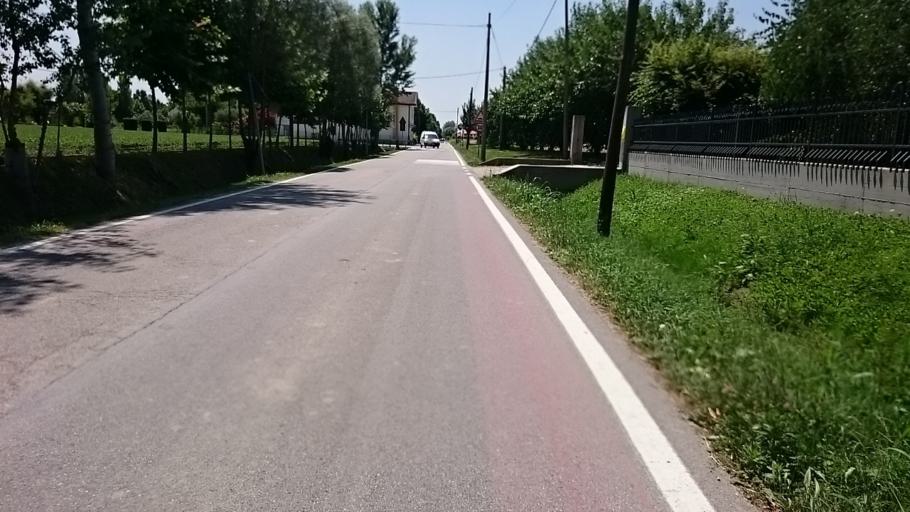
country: IT
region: Veneto
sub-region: Provincia di Padova
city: Villanova
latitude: 45.5083
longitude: 11.9844
